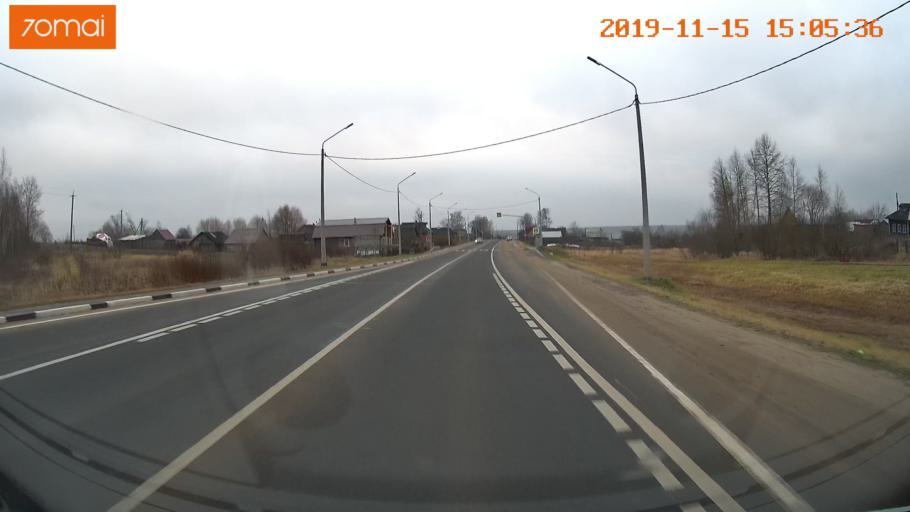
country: RU
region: Jaroslavl
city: Prechistoye
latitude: 58.4016
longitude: 40.3221
